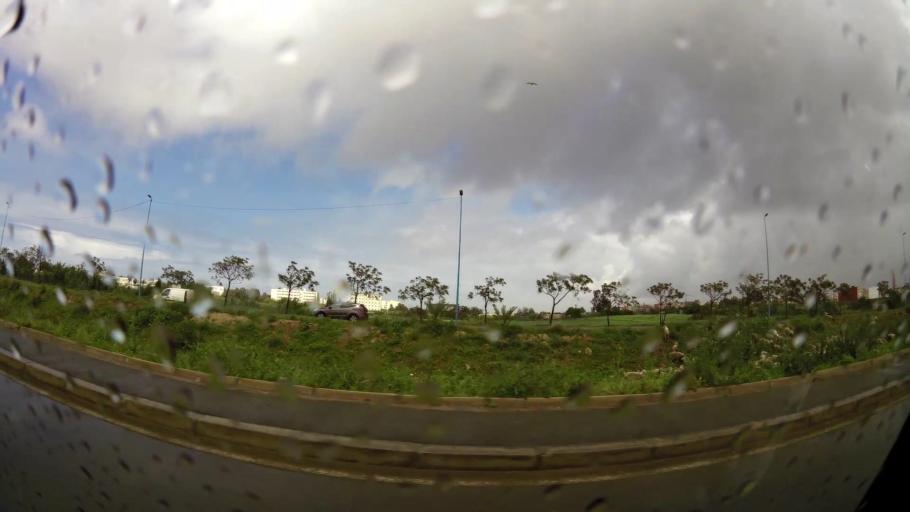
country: MA
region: Grand Casablanca
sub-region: Casablanca
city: Casablanca
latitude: 33.5352
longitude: -7.6578
